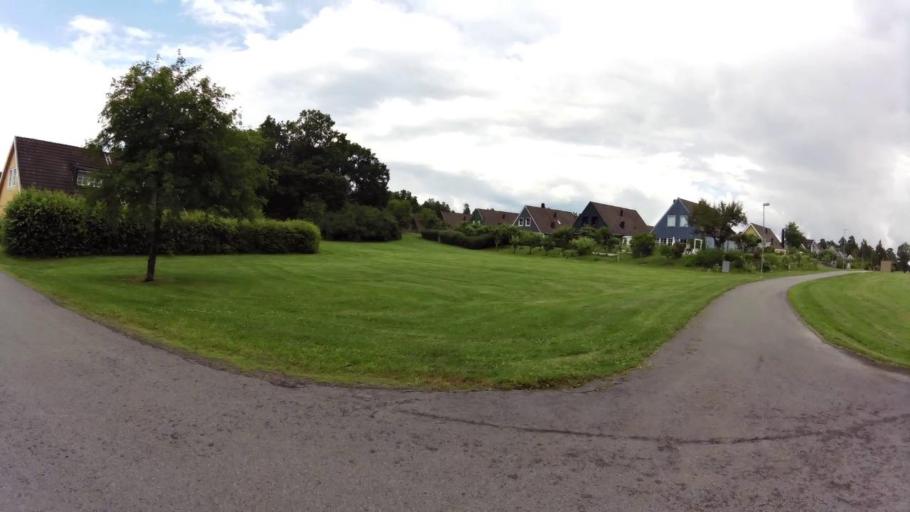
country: SE
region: OEstergoetland
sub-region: Linkopings Kommun
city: Sturefors
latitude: 58.3876
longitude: 15.6989
